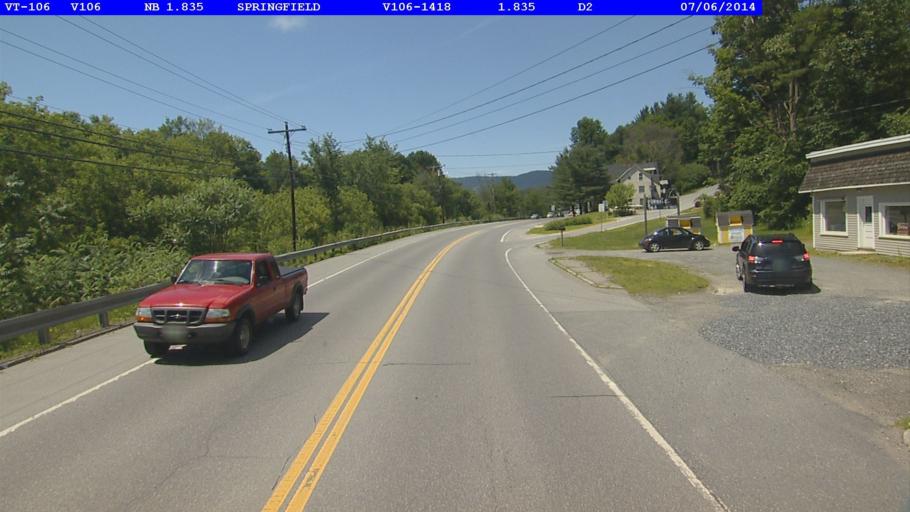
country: US
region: Vermont
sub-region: Windsor County
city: Springfield
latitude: 43.3262
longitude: -72.5109
